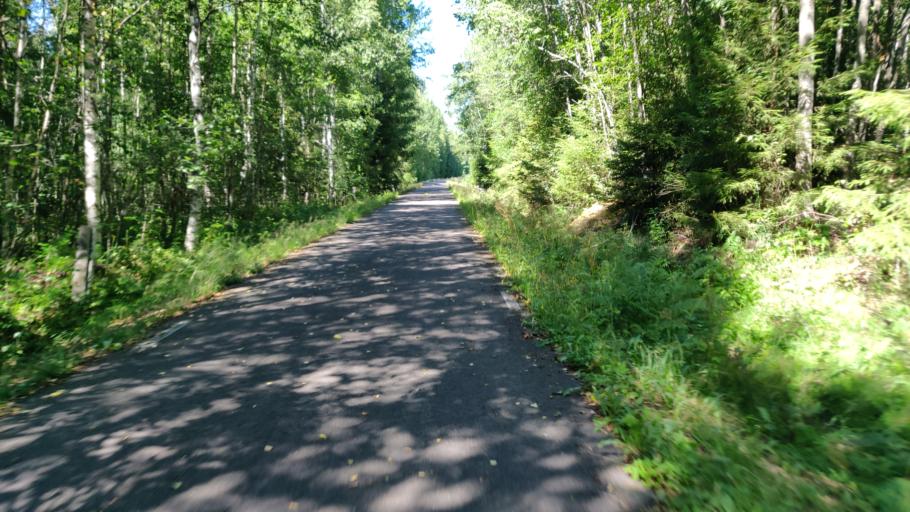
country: SE
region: Vaermland
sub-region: Hagfors Kommun
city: Hagfors
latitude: 59.9594
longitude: 13.5729
